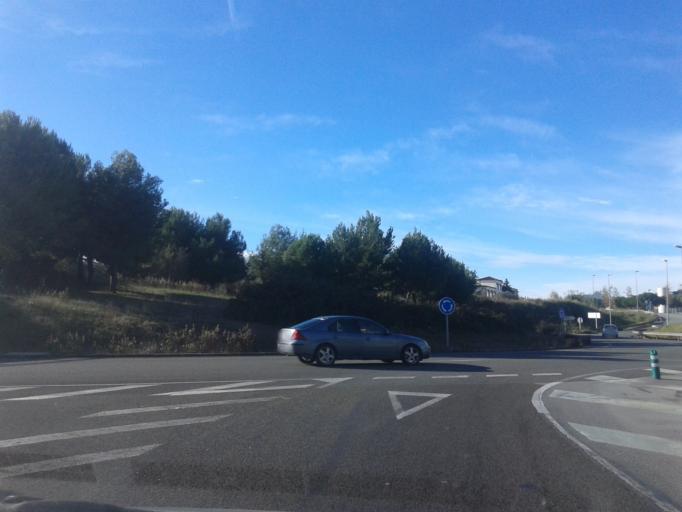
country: ES
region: Catalonia
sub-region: Provincia de Barcelona
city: Vilafranca del Penedes
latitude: 41.3493
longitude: 1.7159
